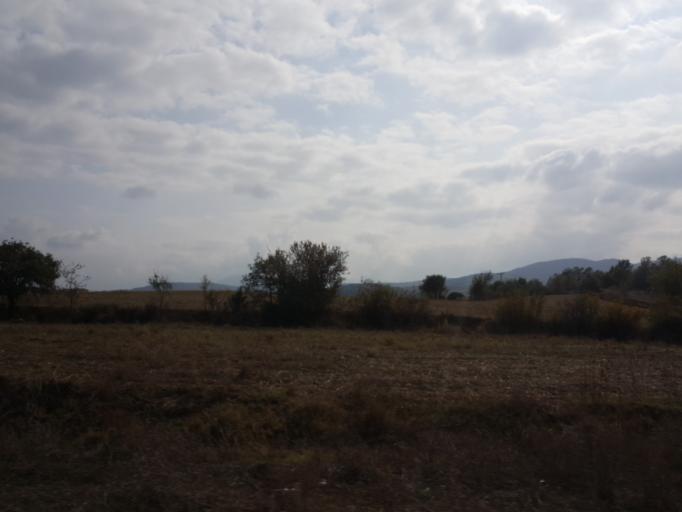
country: TR
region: Sinop
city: Sarayduzu
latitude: 41.3336
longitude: 34.8559
